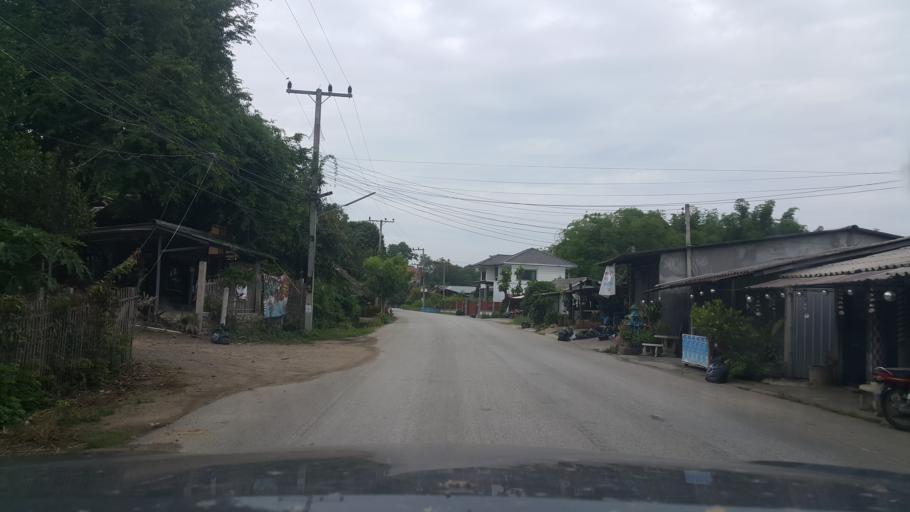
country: TH
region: Chiang Mai
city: San Pa Tong
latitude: 18.6592
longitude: 98.8353
